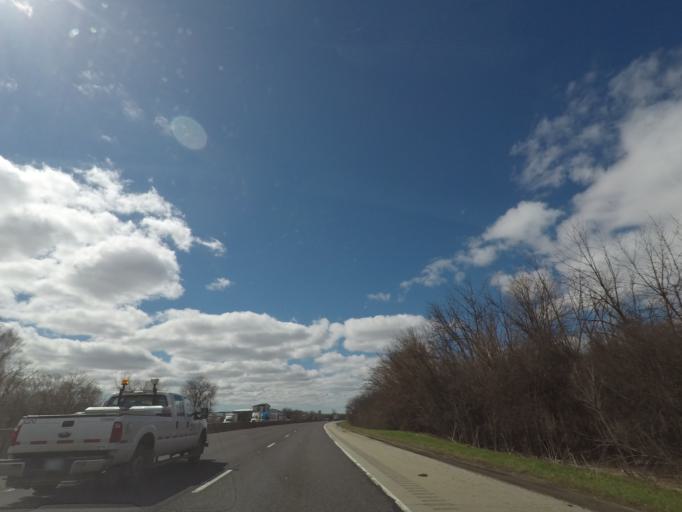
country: US
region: Illinois
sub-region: Will County
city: Shorewood
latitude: 41.5348
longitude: -88.1805
